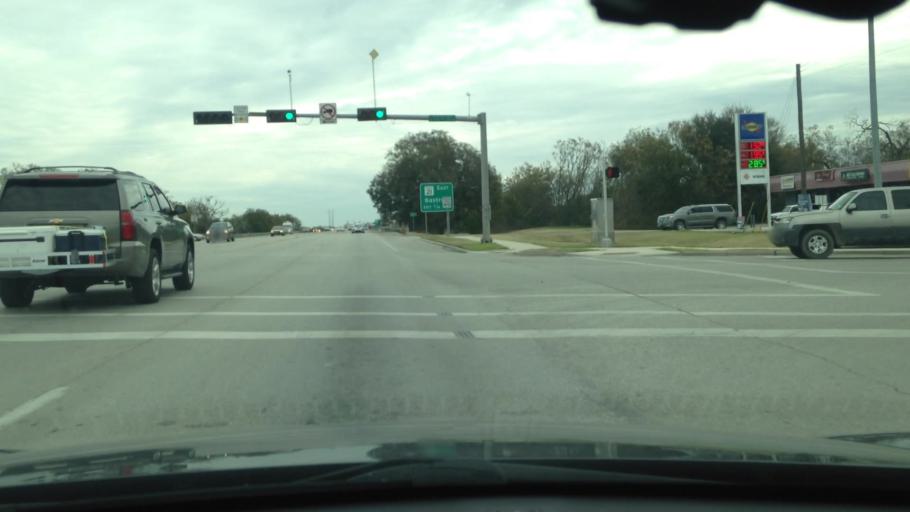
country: US
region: Texas
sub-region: Hays County
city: San Marcos
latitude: 29.8807
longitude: -97.9133
